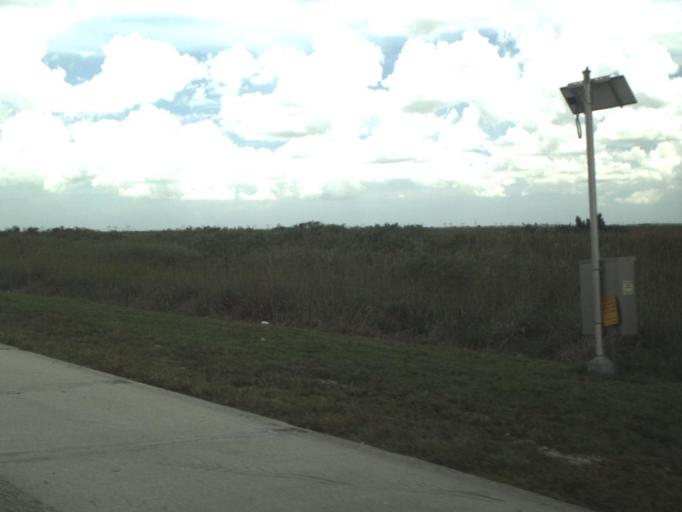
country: US
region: Florida
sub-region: Broward County
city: Weston
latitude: 26.1459
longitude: -80.4811
